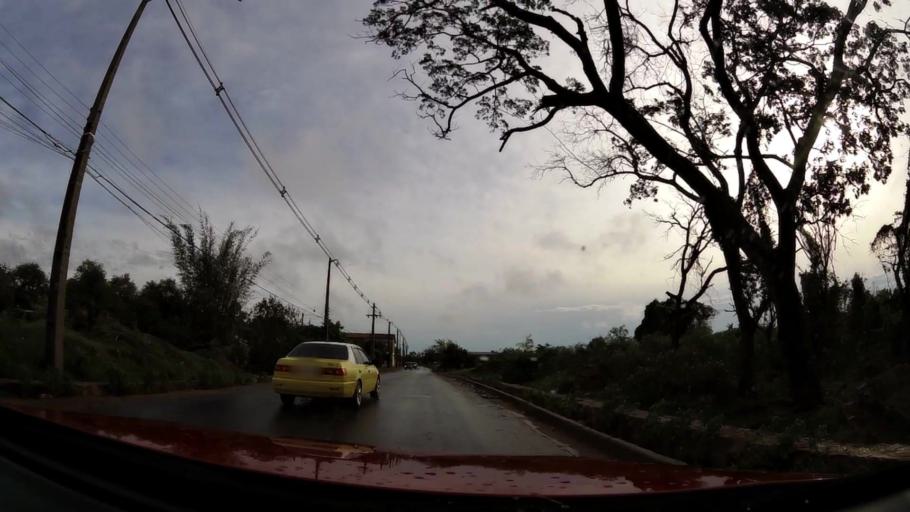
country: PY
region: Central
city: Limpio
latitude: -25.2053
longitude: -57.5048
